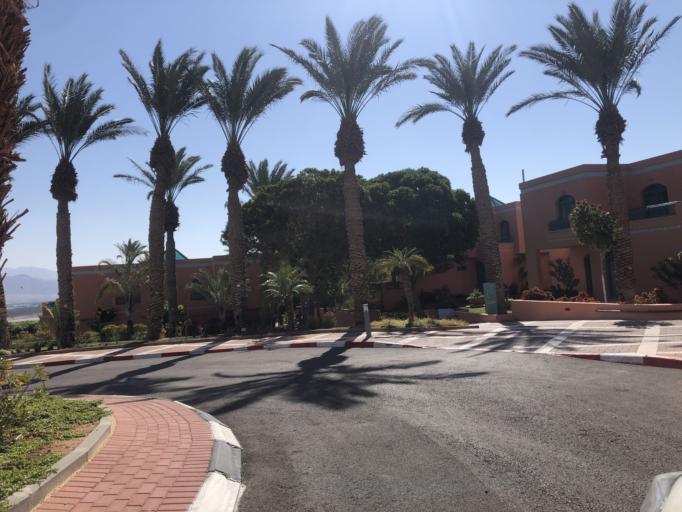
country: IL
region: Southern District
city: Eilat
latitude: 29.5803
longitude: 34.9630
